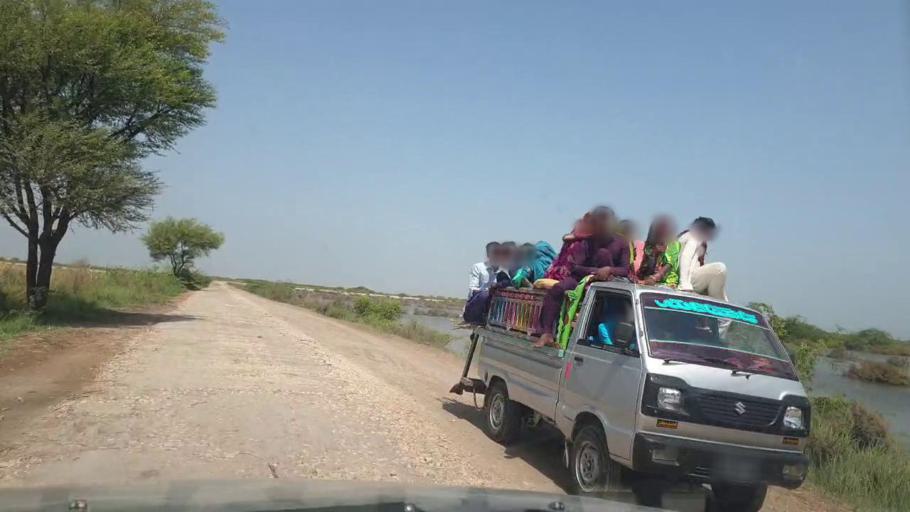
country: PK
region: Sindh
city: Tando Ghulam Ali
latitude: 25.1110
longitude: 68.8021
